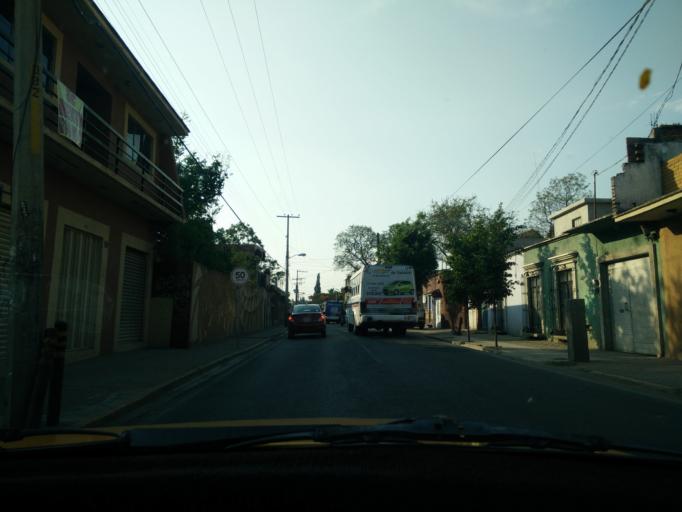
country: MX
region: Oaxaca
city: Oaxaca de Juarez
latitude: 17.0713
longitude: -96.7368
